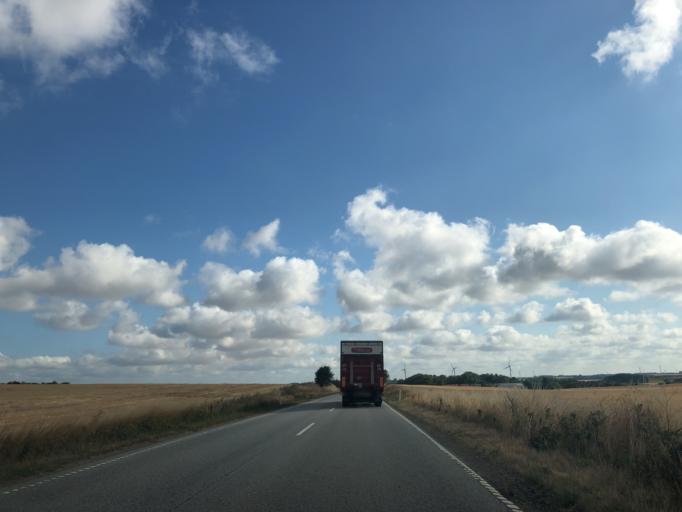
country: DK
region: Central Jutland
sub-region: Skive Kommune
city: Skive
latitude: 56.6588
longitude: 8.9399
